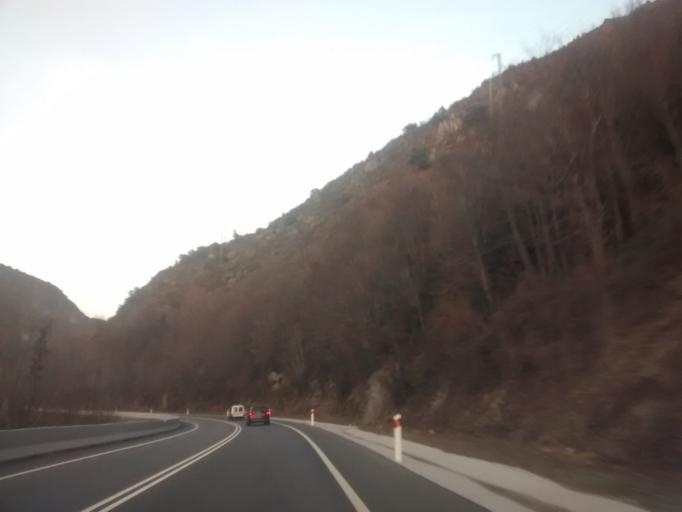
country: ES
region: Catalonia
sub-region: Provincia de Lleida
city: la Seu d'Urgell
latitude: 42.3897
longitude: 1.4617
